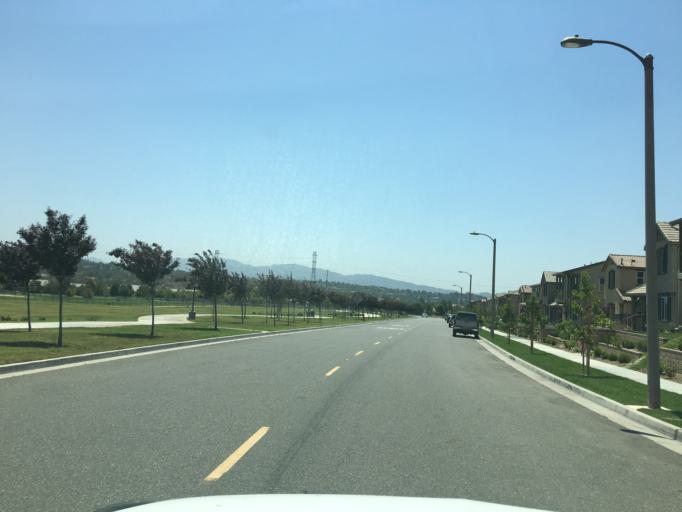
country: US
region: California
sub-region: Los Angeles County
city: Valencia
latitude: 34.4590
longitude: -118.5620
